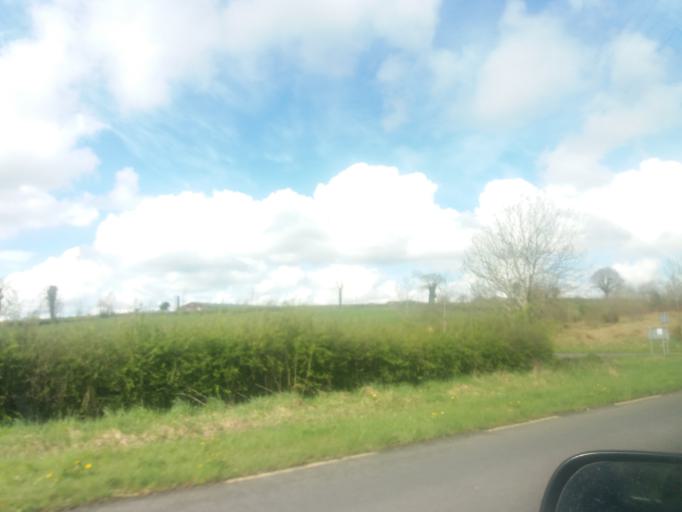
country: IE
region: Ulster
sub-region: An Cabhan
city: Belturbet
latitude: 54.1180
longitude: -7.4797
